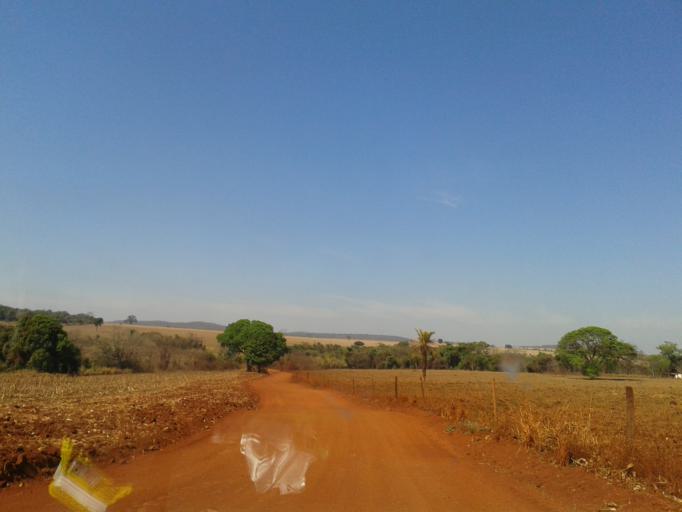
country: BR
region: Minas Gerais
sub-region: Capinopolis
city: Capinopolis
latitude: -18.6062
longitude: -49.4957
